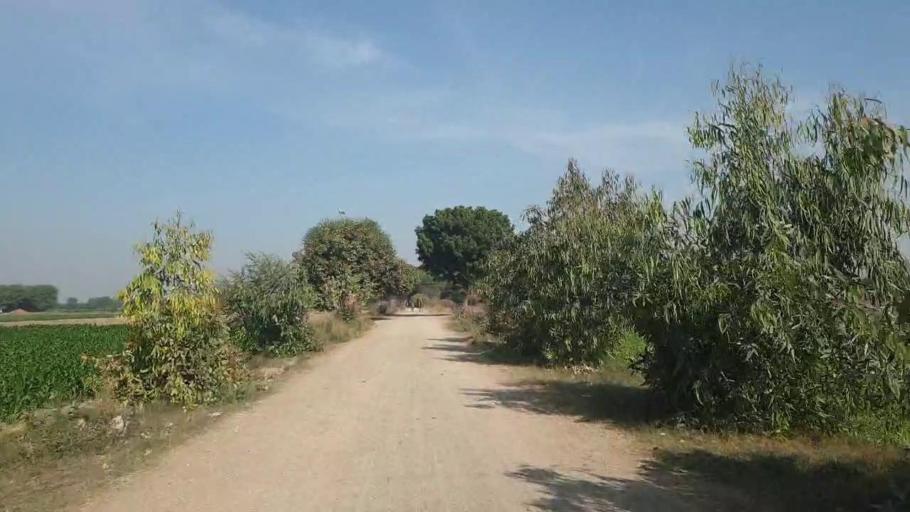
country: PK
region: Sindh
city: Matiari
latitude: 25.6772
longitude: 68.3478
